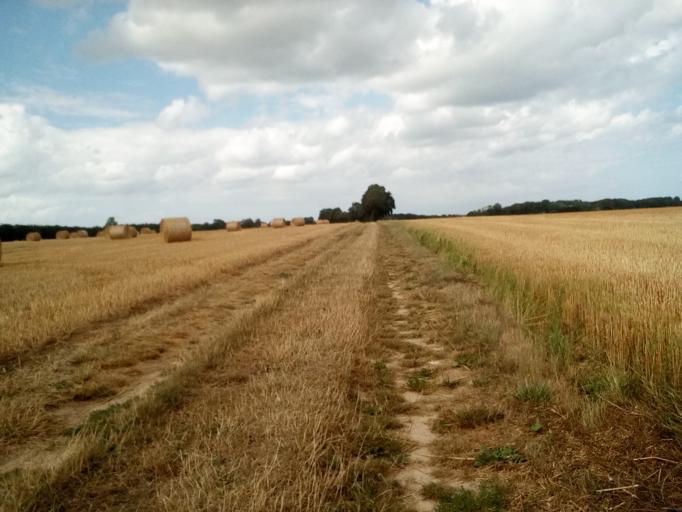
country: FR
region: Lower Normandy
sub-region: Departement du Calvados
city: Creully
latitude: 49.2973
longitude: -0.5699
